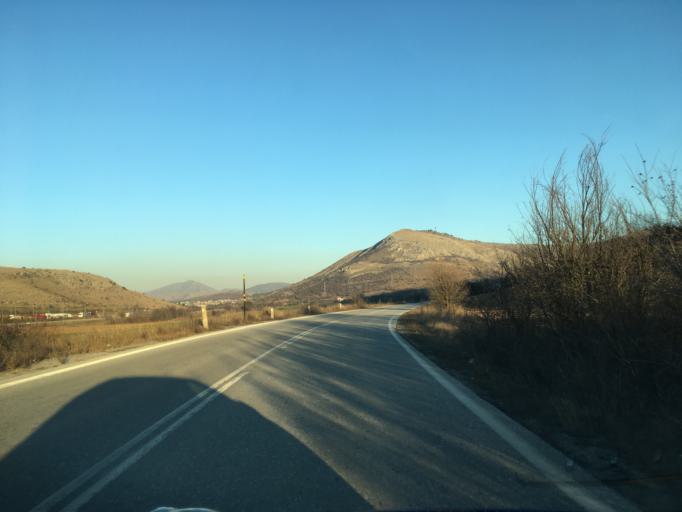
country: GR
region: West Macedonia
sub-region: Nomos Kozanis
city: Kozani
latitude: 40.3174
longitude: 21.7458
